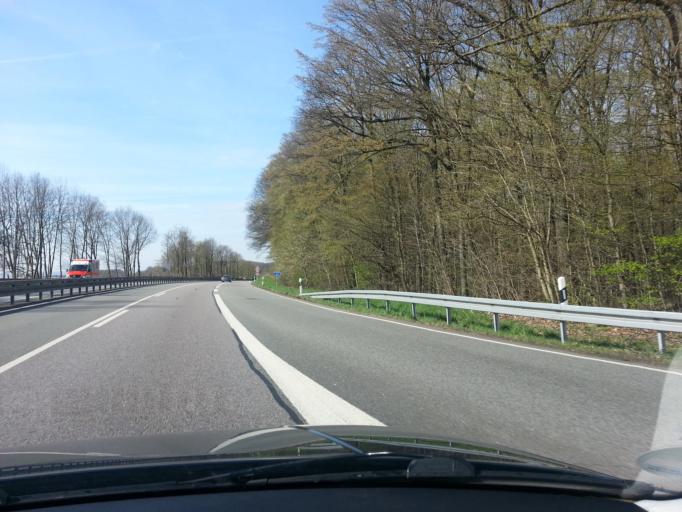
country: DE
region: Saarland
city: Sulzbach
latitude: 49.2920
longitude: 7.0273
